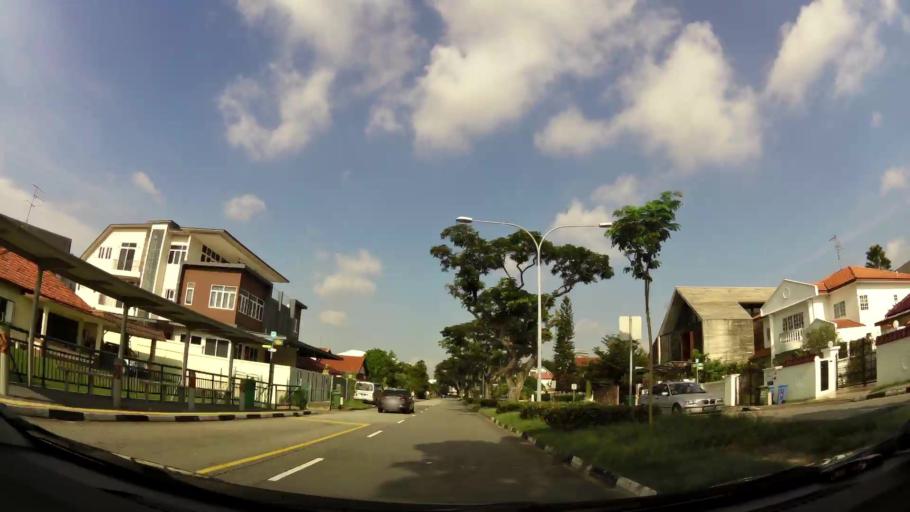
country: SG
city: Singapore
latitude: 1.3167
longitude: 103.9176
